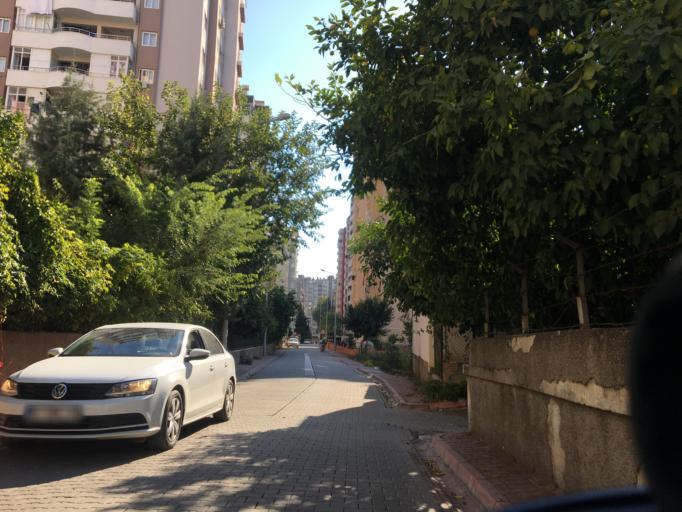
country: TR
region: Adana
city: Seyhan
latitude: 37.0256
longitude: 35.2857
